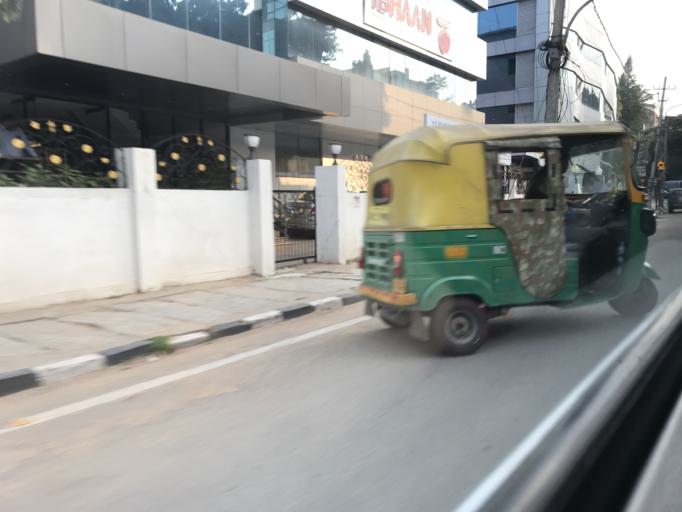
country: IN
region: Karnataka
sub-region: Bangalore Urban
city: Bangalore
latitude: 12.9913
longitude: 77.5886
